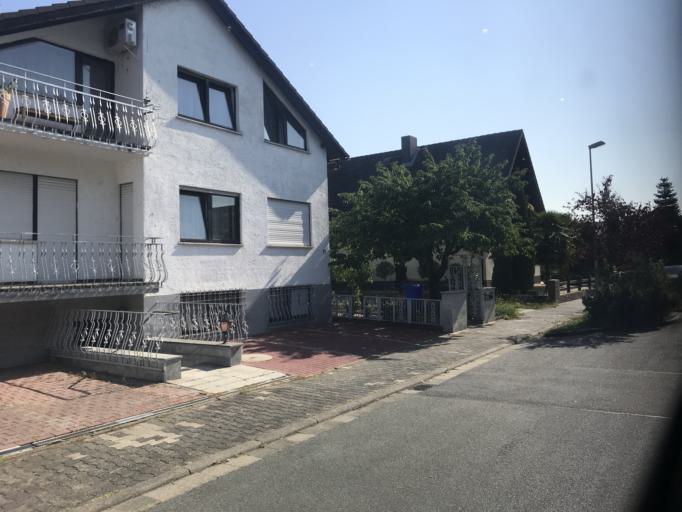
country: DE
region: Hesse
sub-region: Regierungsbezirk Darmstadt
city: Ginsheim-Gustavsburg
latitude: 49.9895
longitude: 8.3473
